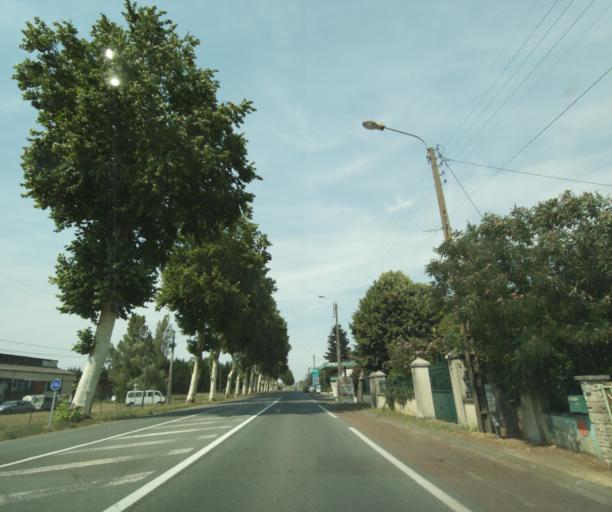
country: FR
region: Centre
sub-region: Departement d'Indre-et-Loire
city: La Celle-Saint-Avant
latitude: 47.0107
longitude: 0.6014
